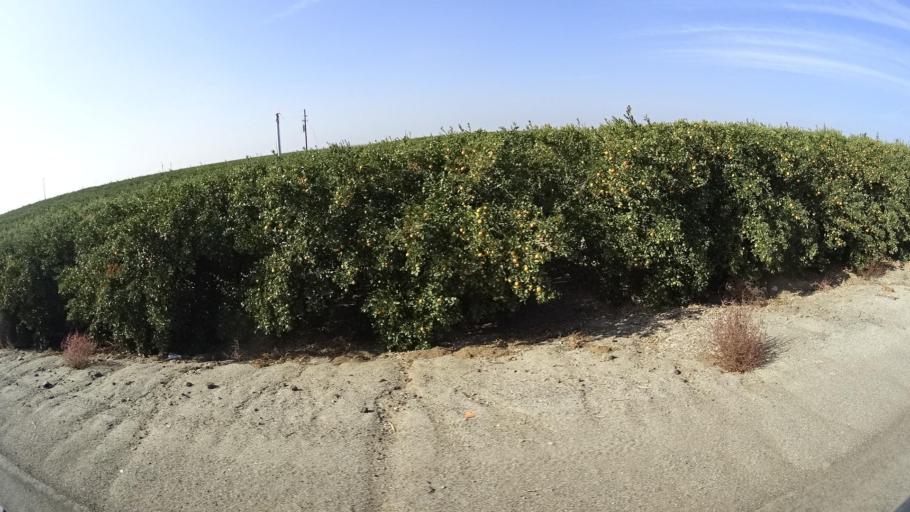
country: US
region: California
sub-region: Kern County
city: McFarland
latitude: 35.6378
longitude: -119.1335
